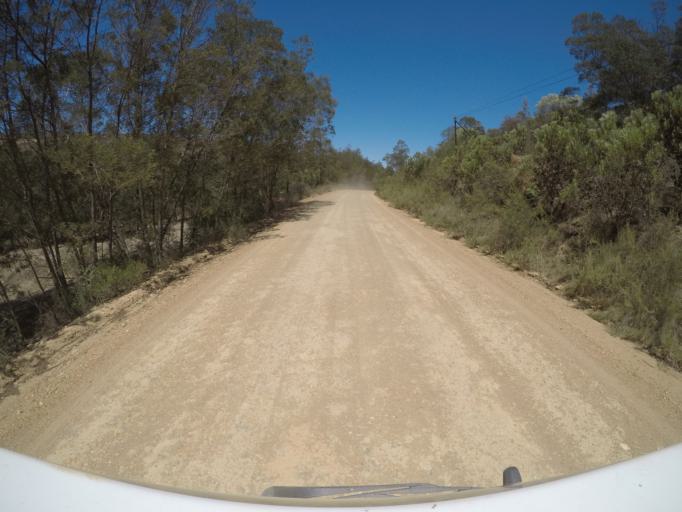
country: ZA
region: Western Cape
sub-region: Overberg District Municipality
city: Caledon
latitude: -34.1543
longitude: 19.2318
